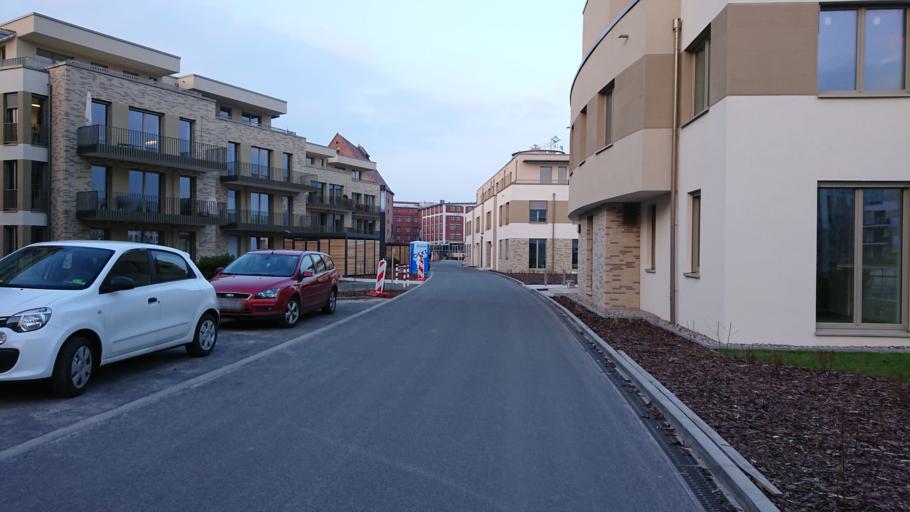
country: DE
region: Berlin
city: Tegel
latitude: 52.5920
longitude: 13.2774
